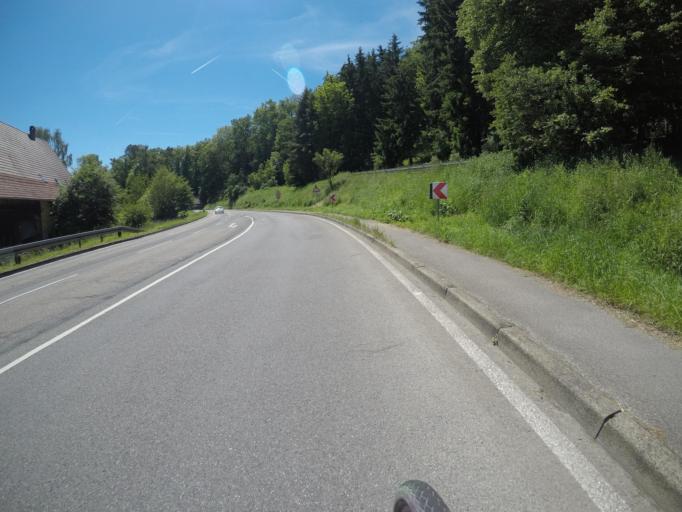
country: DE
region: Baden-Wuerttemberg
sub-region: Karlsruhe Region
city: Simmozheim
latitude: 48.7755
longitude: 8.8361
